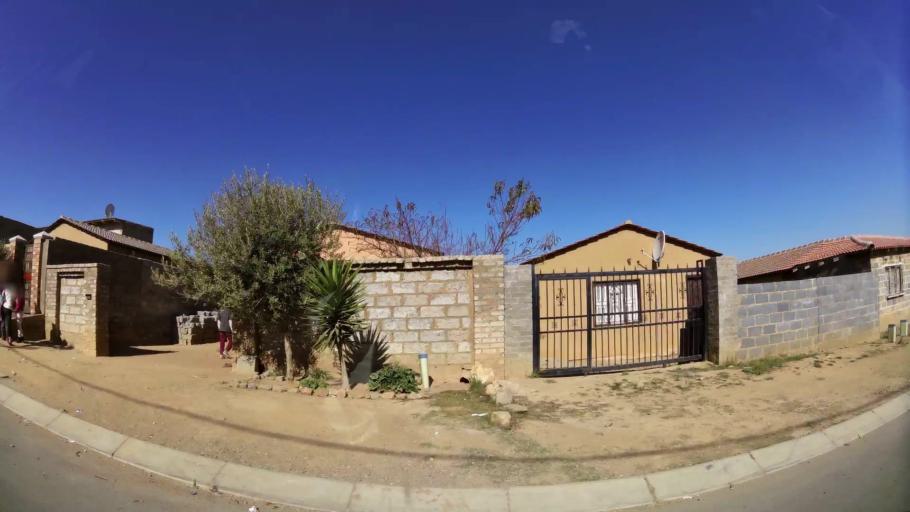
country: ZA
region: Gauteng
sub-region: Ekurhuleni Metropolitan Municipality
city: Tembisa
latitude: -26.0314
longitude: 28.2224
